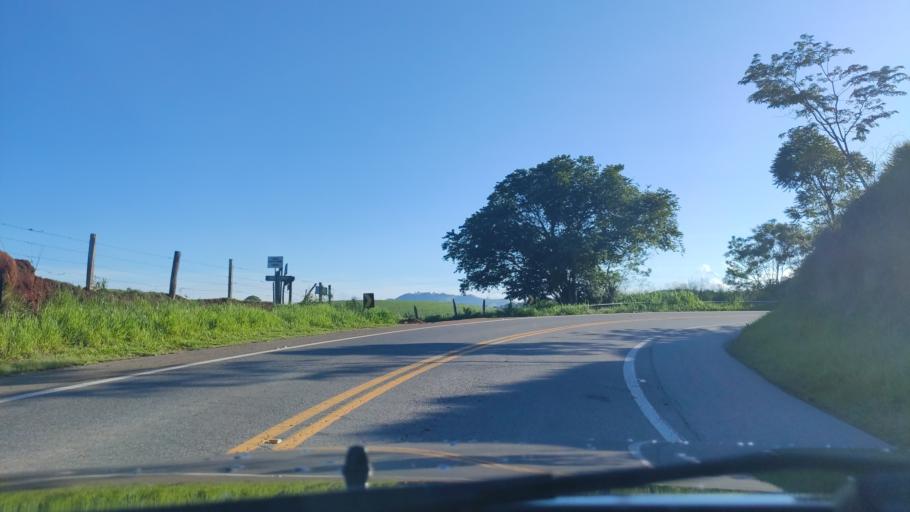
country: BR
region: Sao Paulo
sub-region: Socorro
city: Socorro
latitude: -22.5572
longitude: -46.6043
